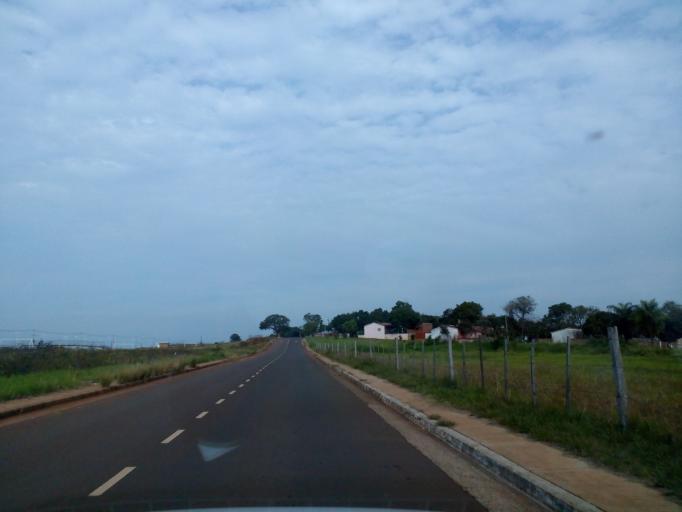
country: AR
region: Misiones
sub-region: Departamento de Capital
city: Posadas
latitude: -27.4182
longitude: -55.8837
